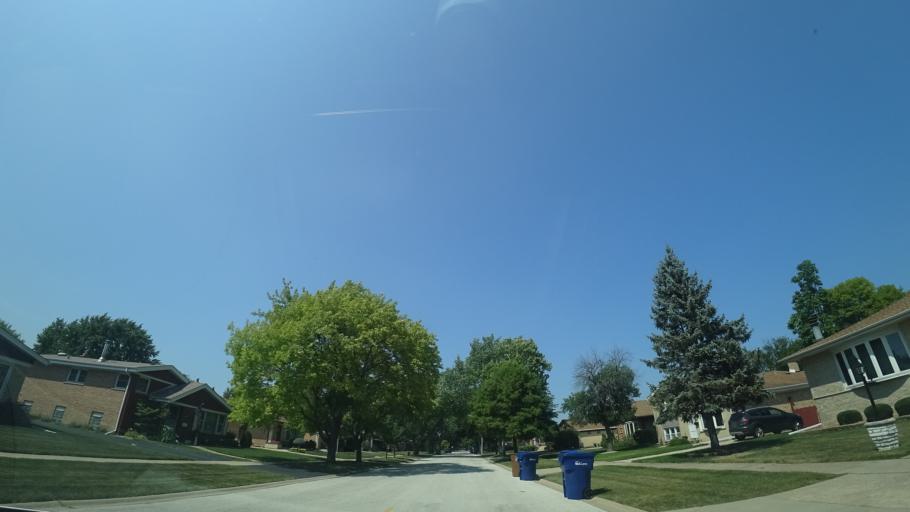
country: US
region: Illinois
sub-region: Cook County
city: Oak Lawn
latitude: 41.6963
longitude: -87.7460
